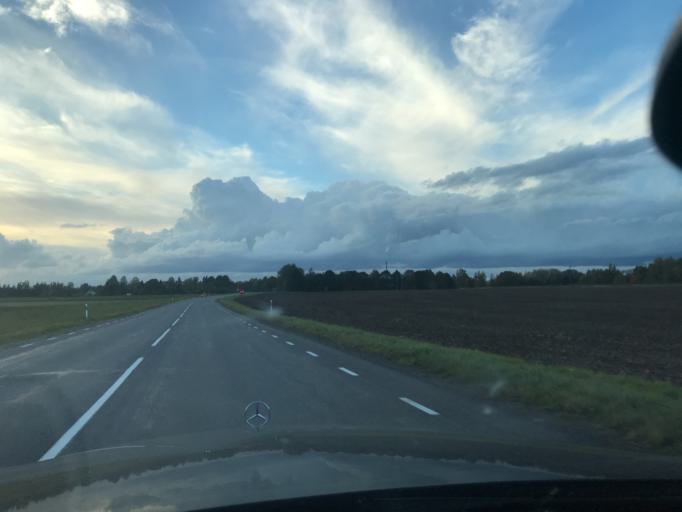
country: EE
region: Vorumaa
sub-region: Antsla vald
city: Vana-Antsla
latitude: 57.8892
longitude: 26.5099
